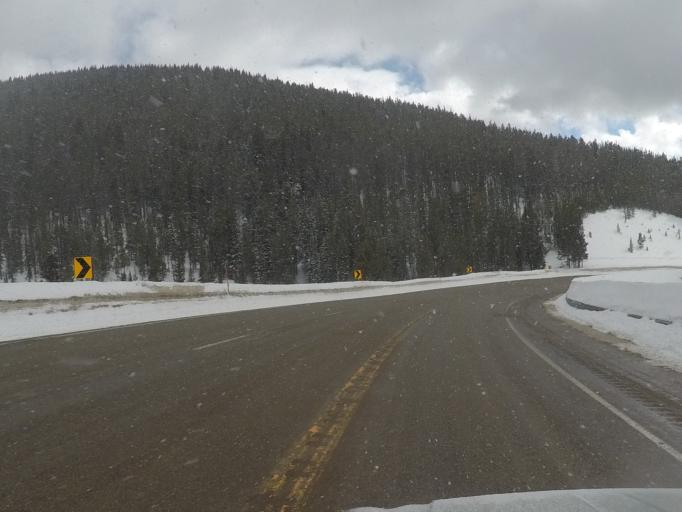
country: US
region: Montana
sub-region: Meagher County
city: White Sulphur Springs
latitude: 46.8268
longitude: -110.6951
